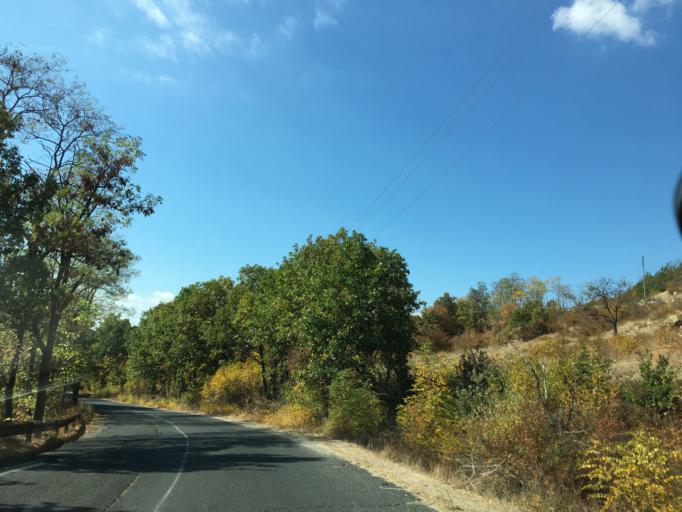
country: BG
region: Kurdzhali
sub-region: Obshtina Kurdzhali
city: Kurdzhali
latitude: 41.5290
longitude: 25.4622
